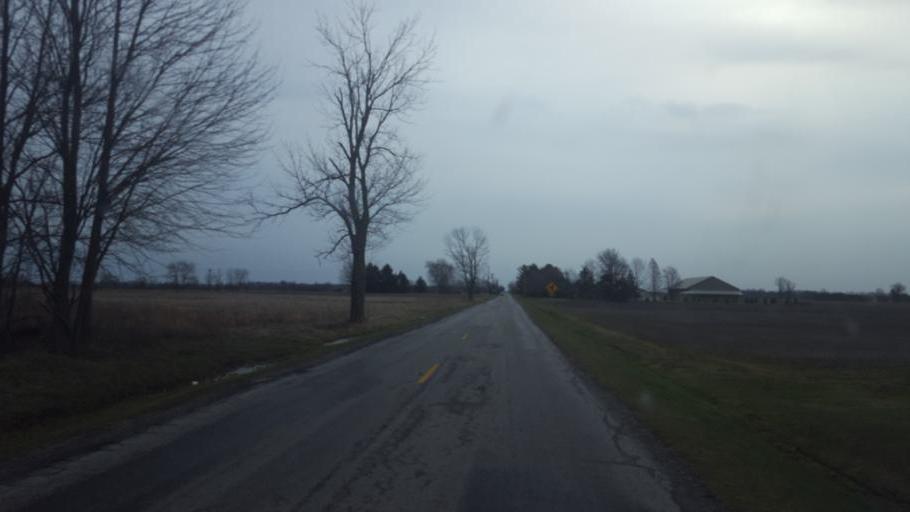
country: US
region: Ohio
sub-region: Marion County
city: Marion
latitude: 40.6522
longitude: -83.0035
